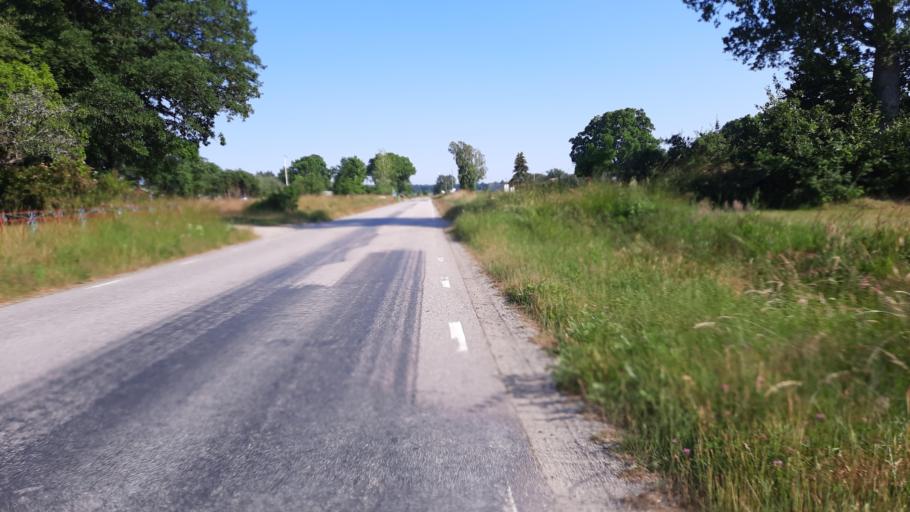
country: SE
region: Blekinge
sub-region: Karlskrona Kommun
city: Sturko
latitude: 56.1075
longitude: 15.6858
